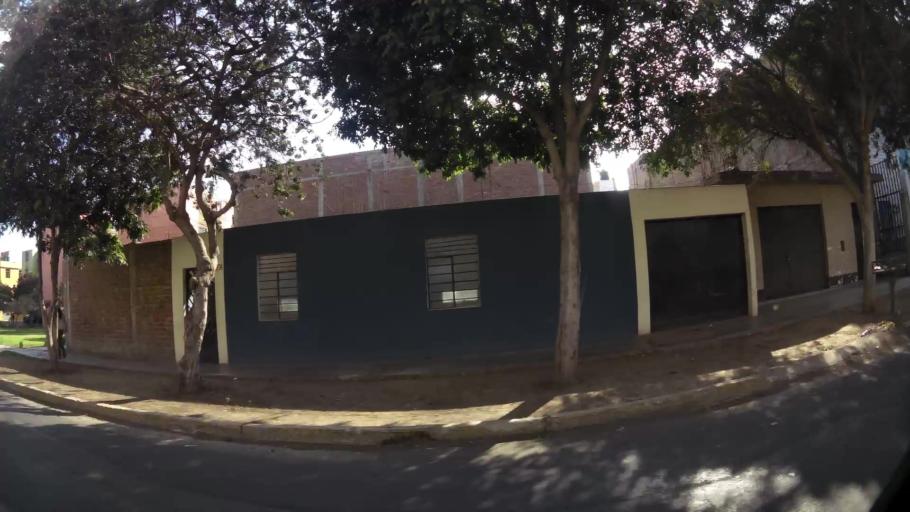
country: PE
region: La Libertad
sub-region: Provincia de Trujillo
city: Trujillo
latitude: -8.1113
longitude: -79.0060
